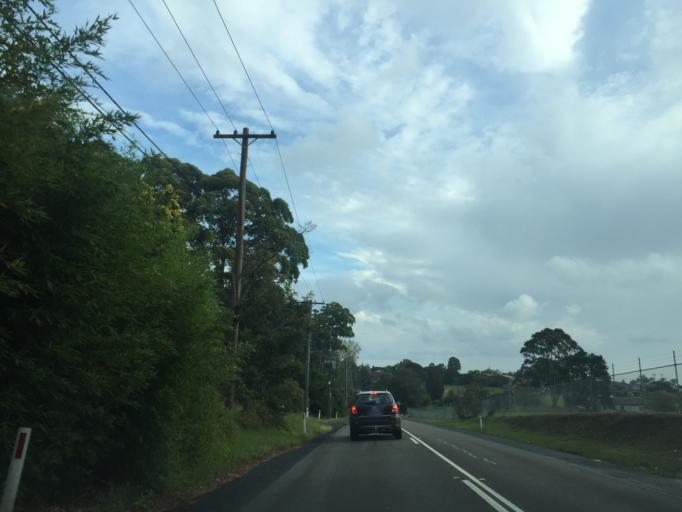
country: AU
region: New South Wales
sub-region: Hornsby Shire
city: Galston
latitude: -33.6769
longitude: 151.0316
